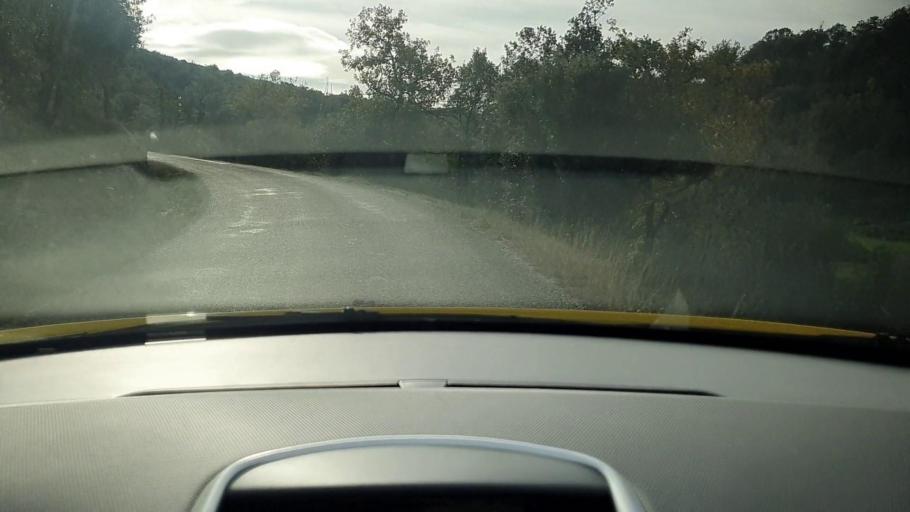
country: FR
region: Languedoc-Roussillon
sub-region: Departement du Gard
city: Saint-Jean-du-Gard
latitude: 44.0581
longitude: 3.9227
